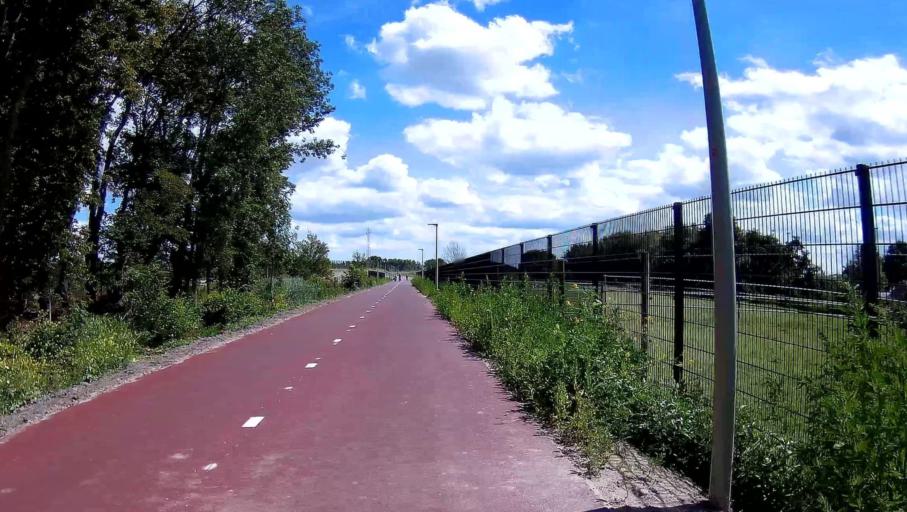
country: NL
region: South Holland
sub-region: Gemeente Leidschendam-Voorburg
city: Voorburg
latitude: 52.0561
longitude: 4.3513
